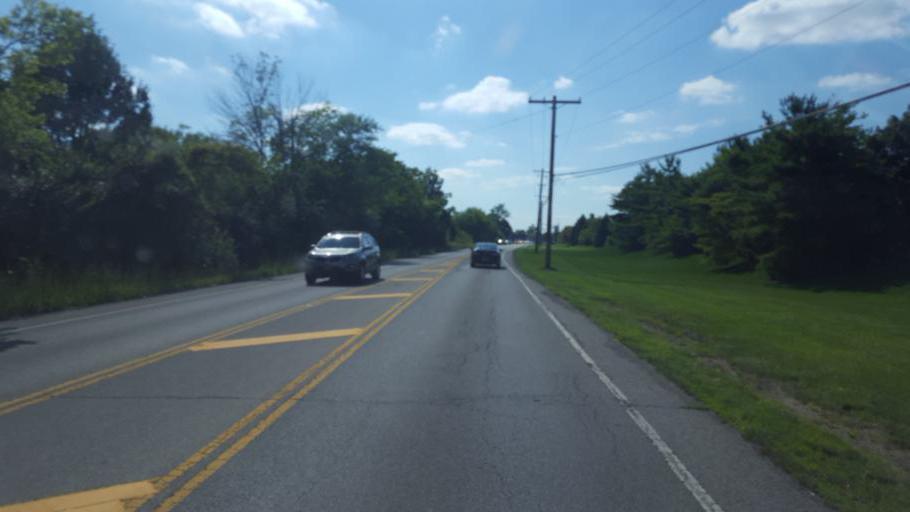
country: US
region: Ohio
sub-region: Franklin County
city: Dublin
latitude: 40.0923
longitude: -83.0787
